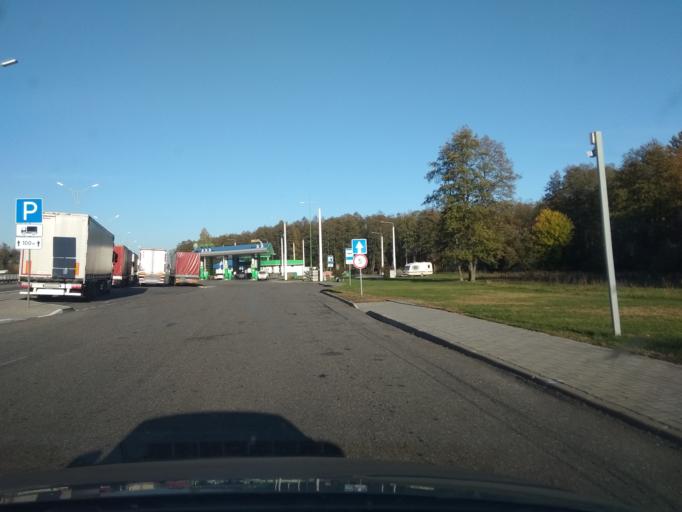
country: BY
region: Brest
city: Ivatsevichy
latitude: 52.6933
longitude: 25.3512
